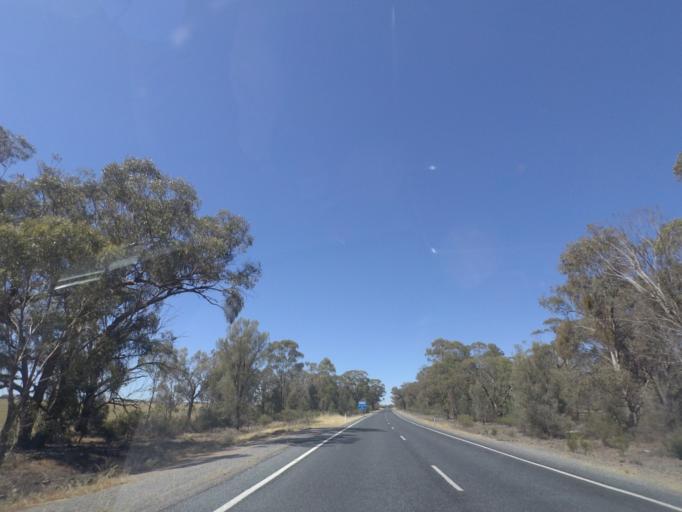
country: AU
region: New South Wales
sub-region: Narrandera
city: Narrandera
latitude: -34.4413
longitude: 146.8412
